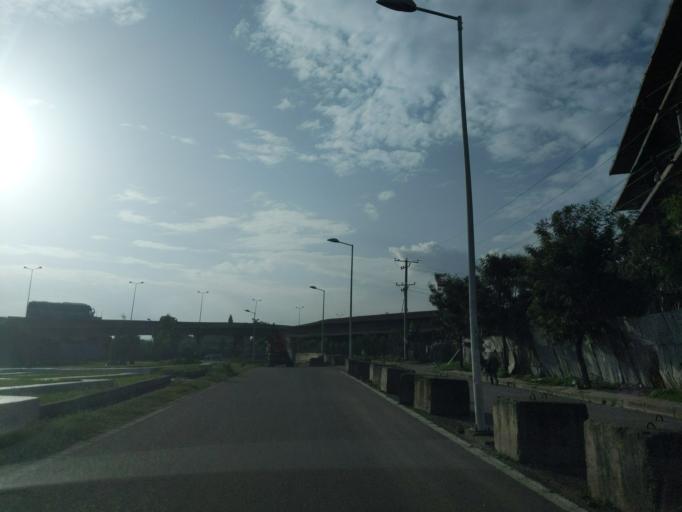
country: ET
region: Adis Abeba
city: Addis Ababa
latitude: 8.9820
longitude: 38.7606
